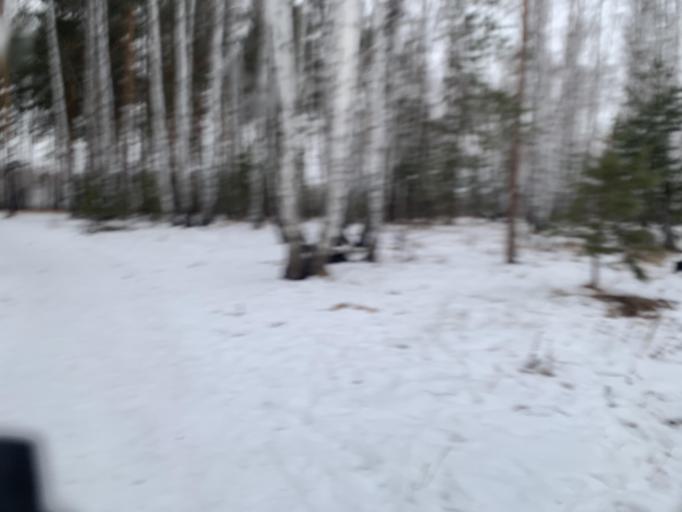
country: RU
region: Chelyabinsk
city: Roshchino
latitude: 55.2028
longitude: 61.2662
